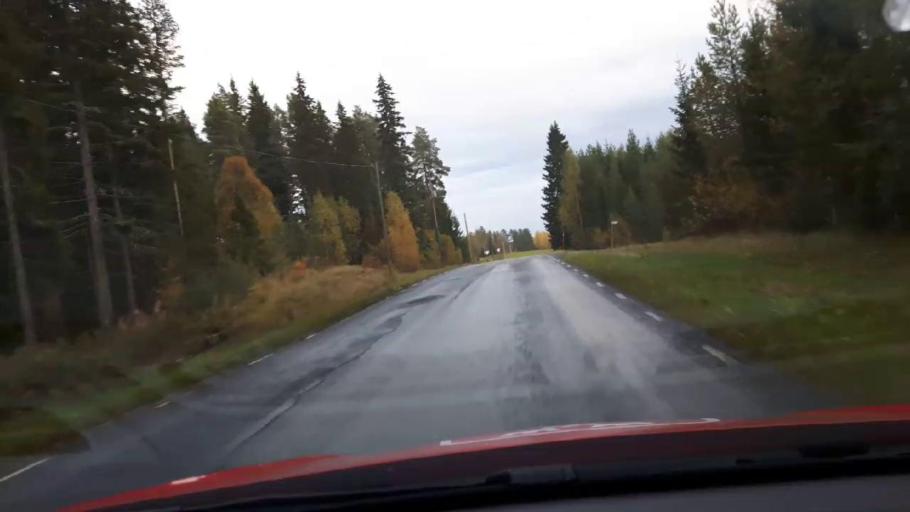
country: SE
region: Jaemtland
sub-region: OEstersunds Kommun
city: Lit
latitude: 63.3221
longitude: 14.9418
